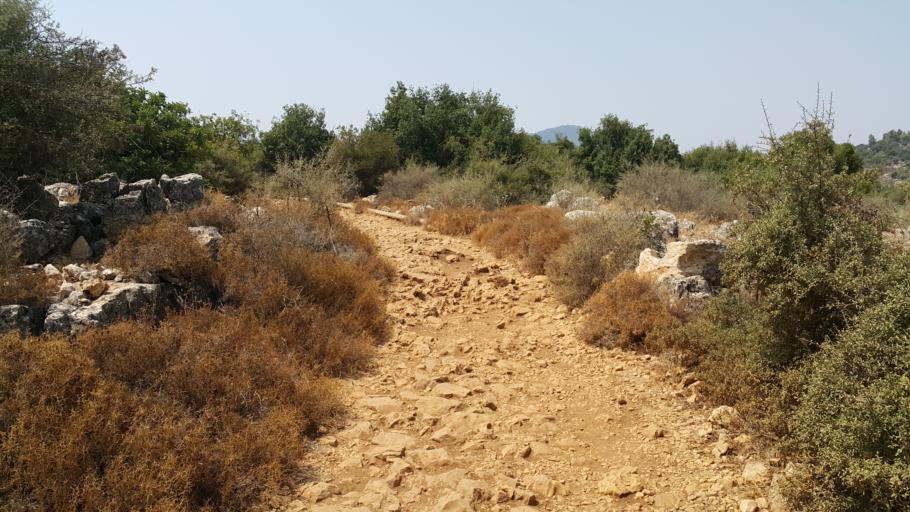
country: IL
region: Northern District
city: Safed
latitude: 32.9742
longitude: 35.4641
